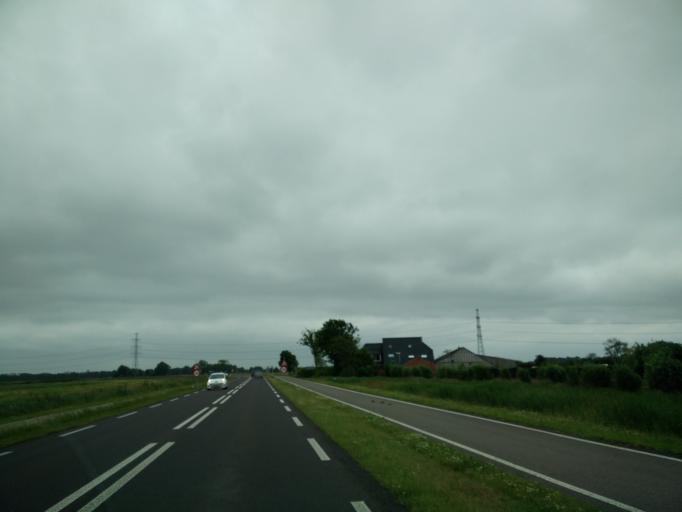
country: NL
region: Groningen
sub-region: Gemeente Groningen
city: Groningen
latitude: 53.1797
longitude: 6.5046
